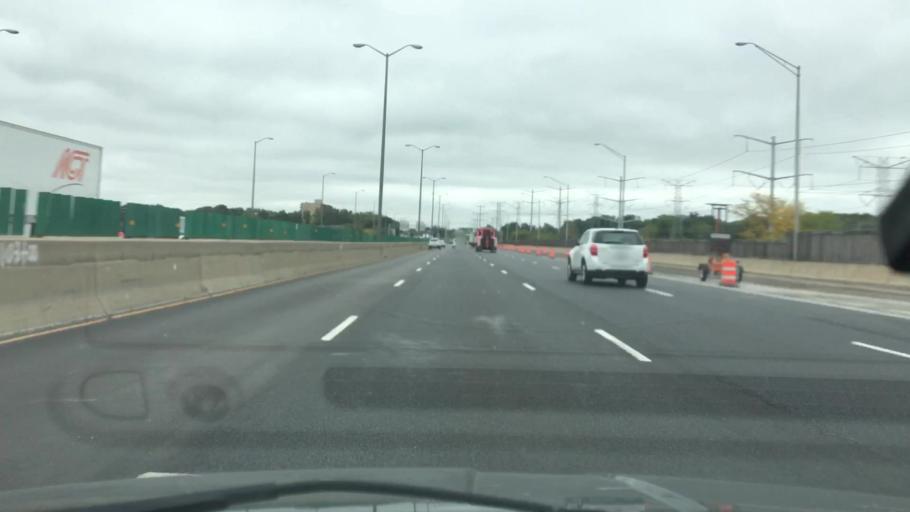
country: US
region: Illinois
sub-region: DuPage County
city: Lisle
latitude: 41.7968
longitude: -88.0570
